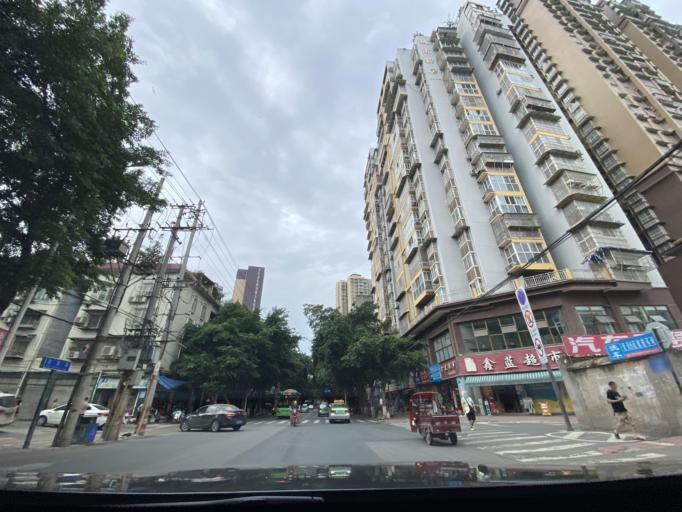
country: CN
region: Sichuan
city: Jiancheng
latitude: 30.3842
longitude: 104.5526
